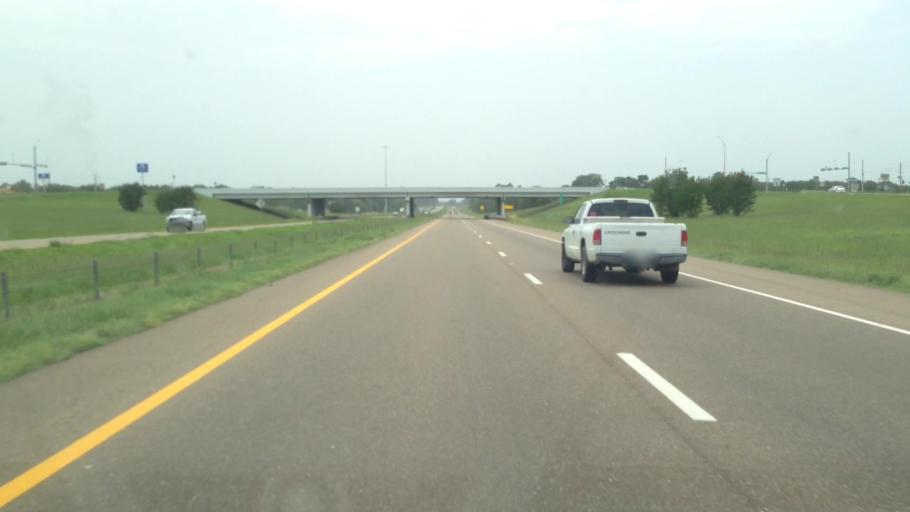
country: US
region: Texas
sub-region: Bowie County
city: New Boston
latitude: 33.4744
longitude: -94.4071
